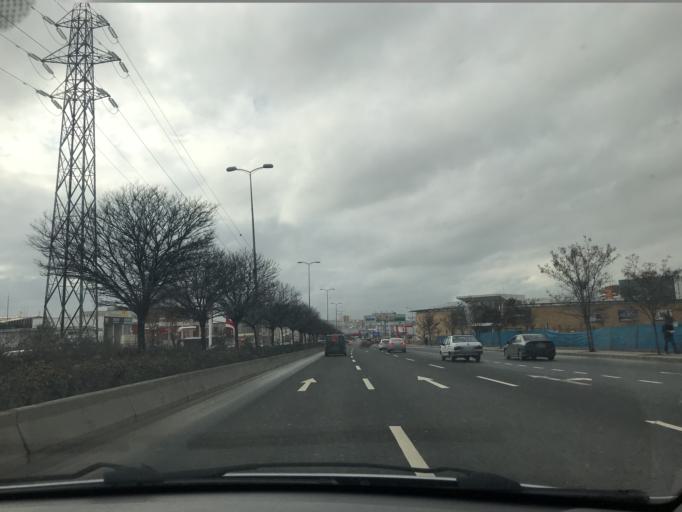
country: TR
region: Ankara
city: Batikent
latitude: 39.9608
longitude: 32.7744
